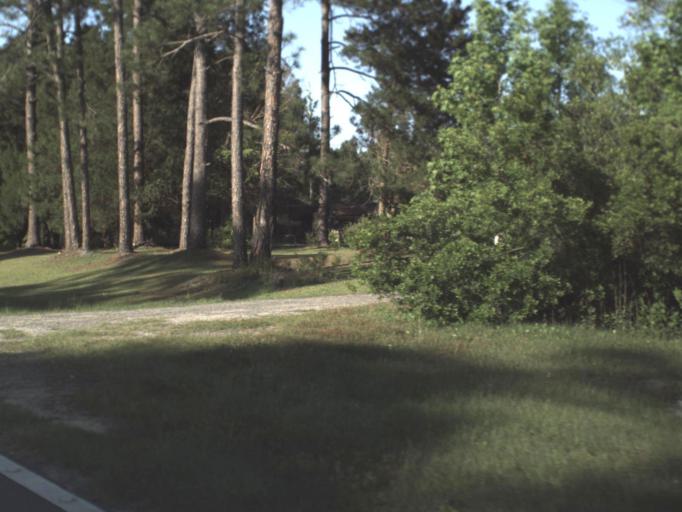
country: US
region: Florida
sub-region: Liberty County
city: Bristol
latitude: 30.3306
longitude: -84.8235
